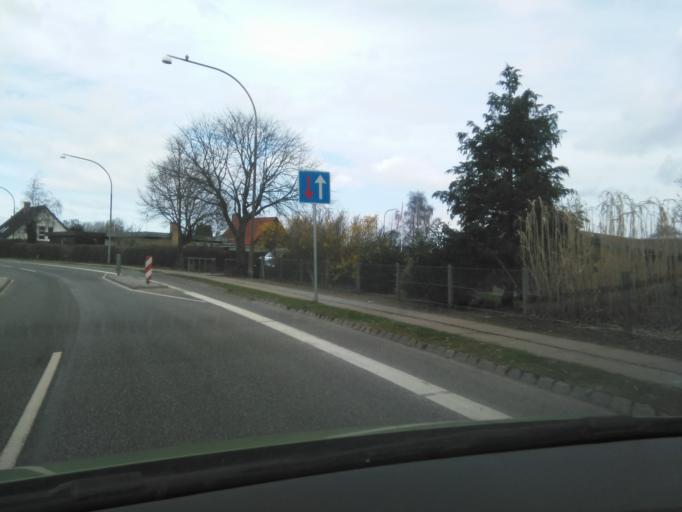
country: DK
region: South Denmark
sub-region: Nordfyns Kommune
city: Bogense
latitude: 55.5649
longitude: 10.0985
